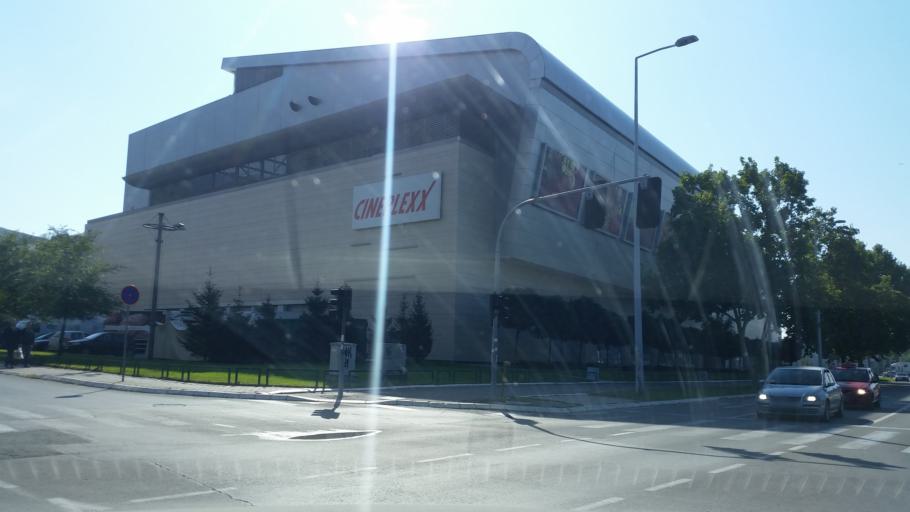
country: RS
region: Central Serbia
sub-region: Belgrade
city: Novi Beograd
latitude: 44.8064
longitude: 20.4036
